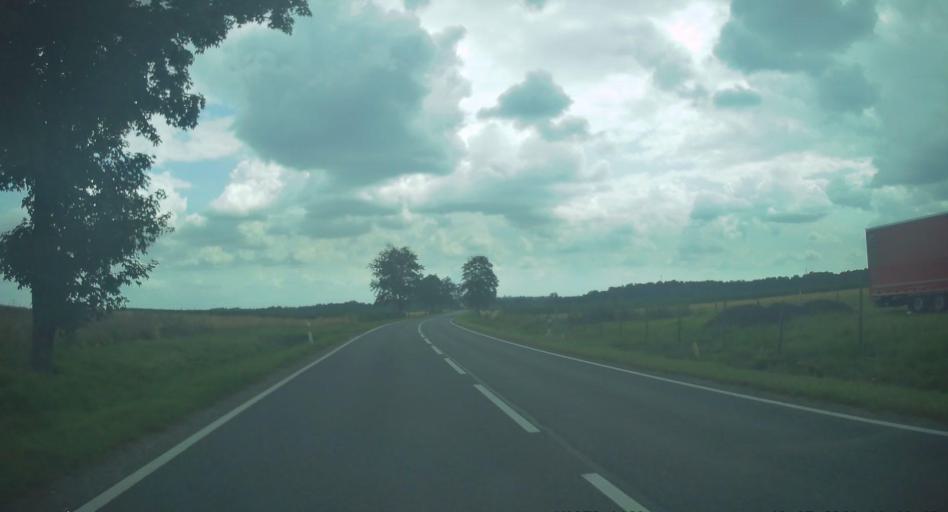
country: PL
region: Opole Voivodeship
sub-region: Powiat prudnicki
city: Laka Prudnicka
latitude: 50.4117
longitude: 17.5003
